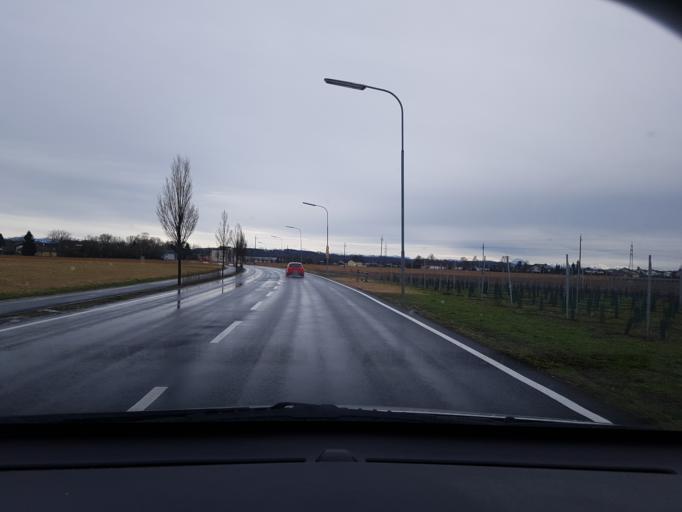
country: AT
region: Upper Austria
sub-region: Politischer Bezirk Linz-Land
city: Traun
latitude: 48.2197
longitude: 14.2191
